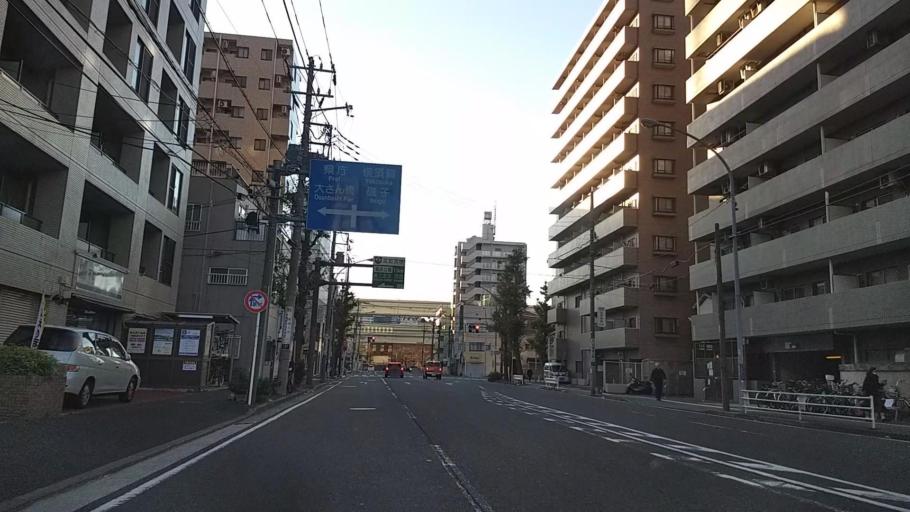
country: JP
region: Kanagawa
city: Yokohama
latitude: 35.4354
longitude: 139.6265
